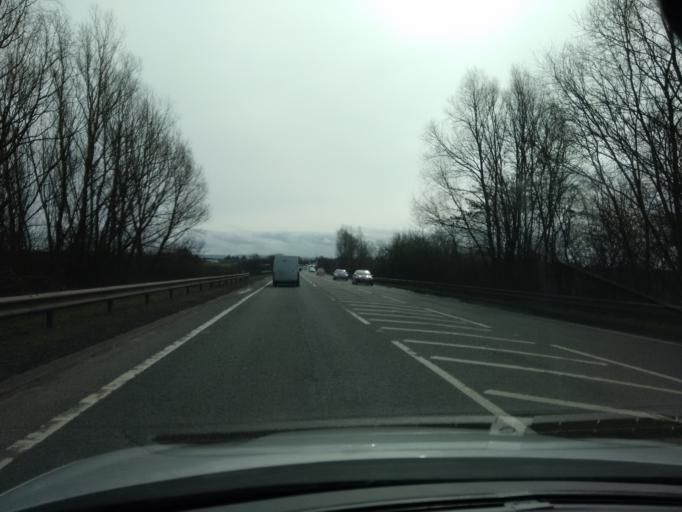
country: GB
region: England
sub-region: Worcestershire
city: Evesham
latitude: 52.1073
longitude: -1.9308
